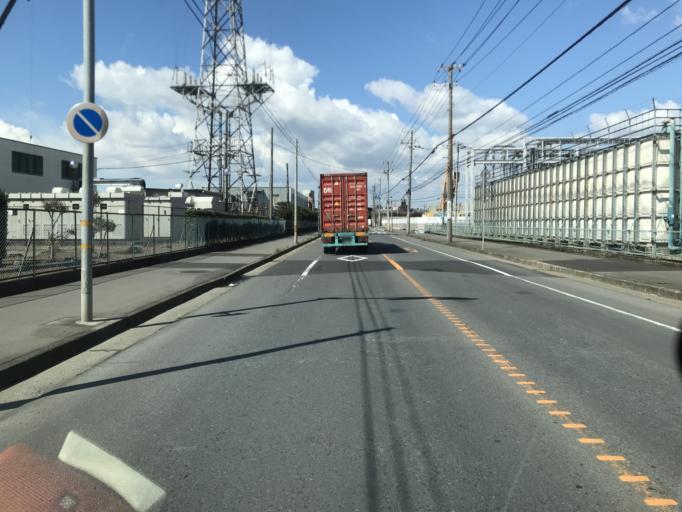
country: JP
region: Ibaraki
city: Ishioka
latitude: 36.1211
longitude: 140.2197
